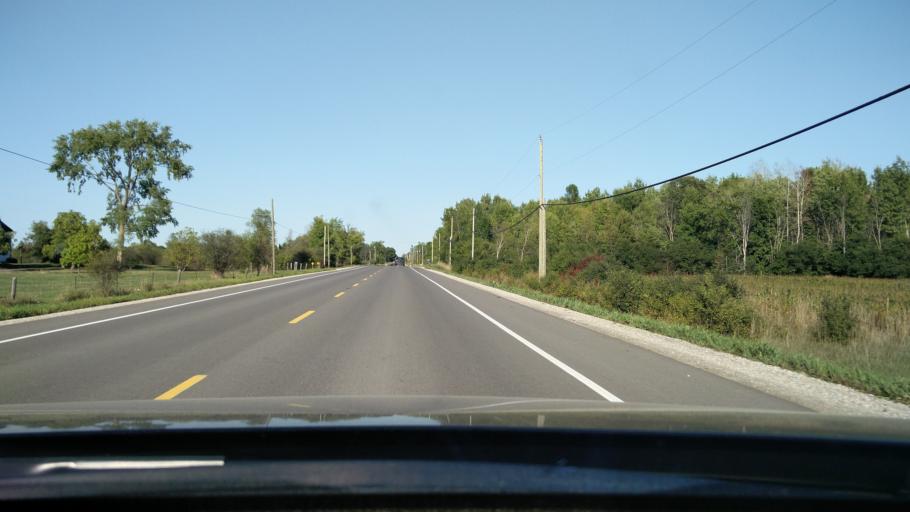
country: CA
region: Ontario
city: Perth
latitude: 44.9187
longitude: -76.2245
